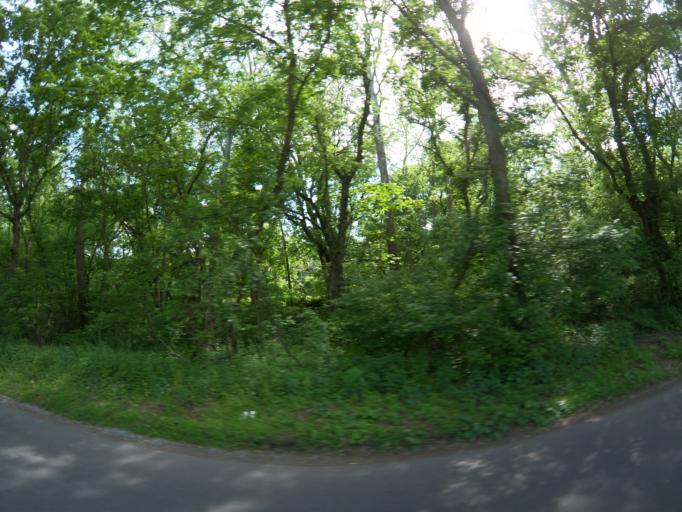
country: US
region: West Virginia
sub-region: Jefferson County
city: Shepherdstown
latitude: 39.4352
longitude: -77.7979
